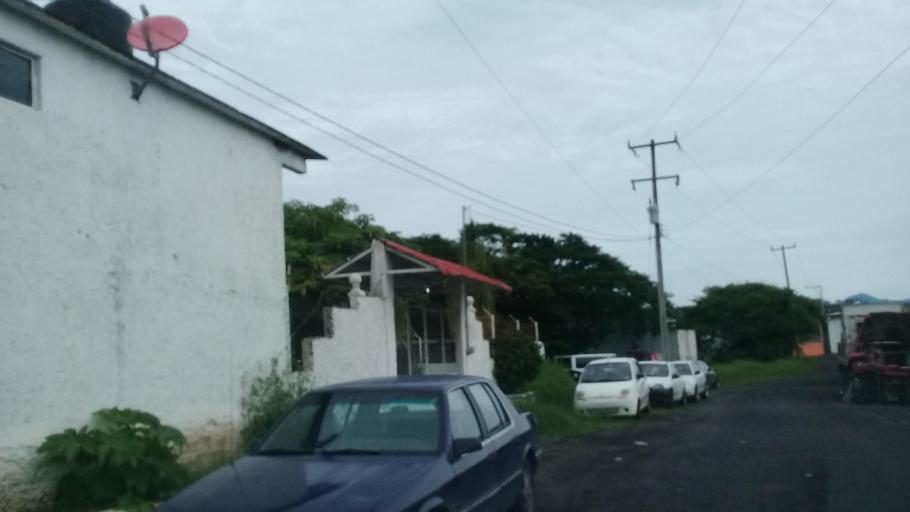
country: MX
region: Veracruz
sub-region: Emiliano Zapata
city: Dos Rios
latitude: 19.4843
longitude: -96.8057
